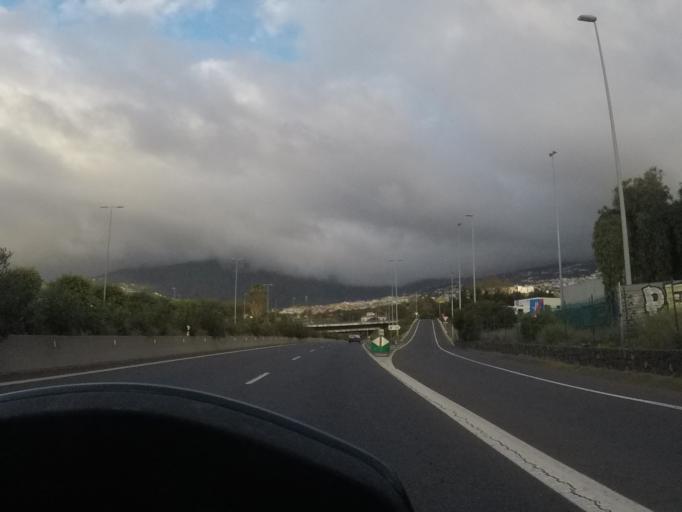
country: ES
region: Canary Islands
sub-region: Provincia de Santa Cruz de Tenerife
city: Puerto de la Cruz
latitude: 28.3974
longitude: -16.5419
